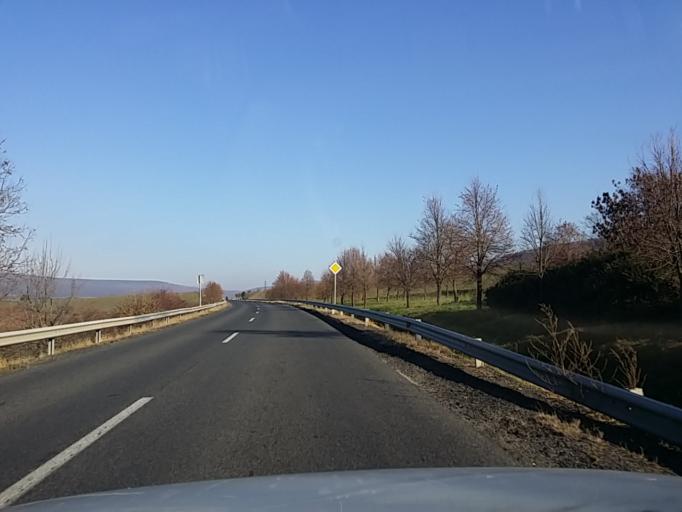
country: HU
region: Veszprem
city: Tapolca
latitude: 46.8967
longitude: 17.5198
